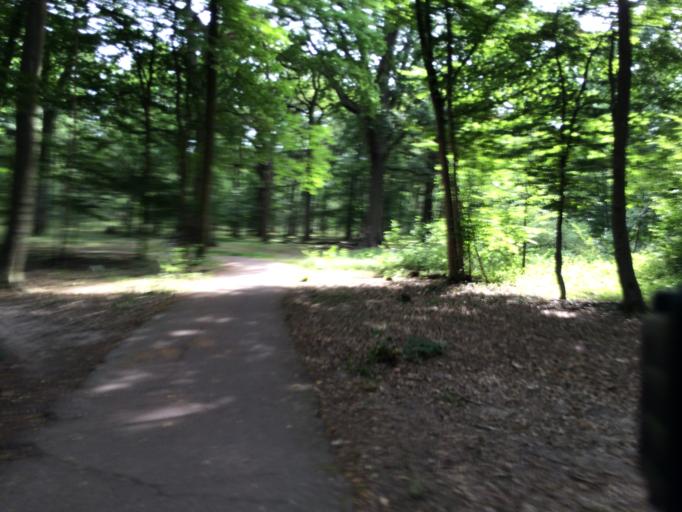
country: FR
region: Ile-de-France
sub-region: Departement de l'Essonne
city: Brunoy
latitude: 48.6755
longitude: 2.4901
